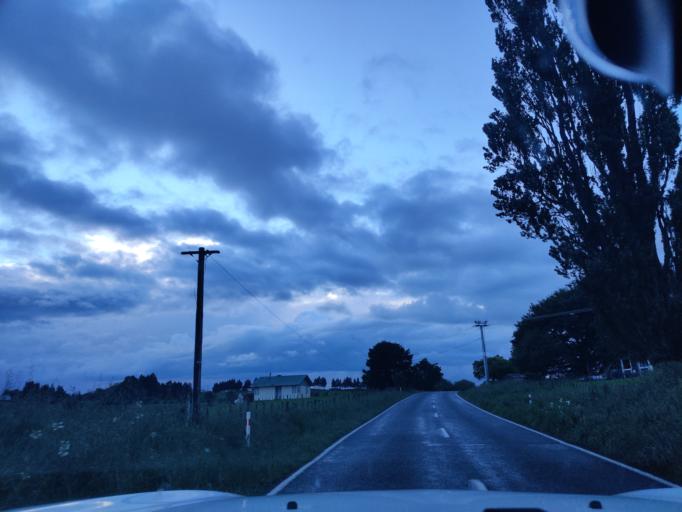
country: NZ
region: Waikato
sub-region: South Waikato District
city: Tokoroa
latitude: -38.1870
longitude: 175.7951
